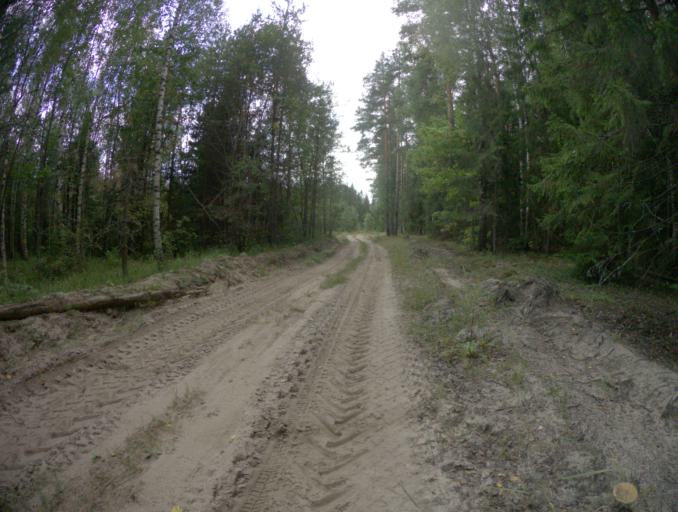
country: RU
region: Vladimir
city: Vorsha
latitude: 55.9564
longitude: 40.1495
